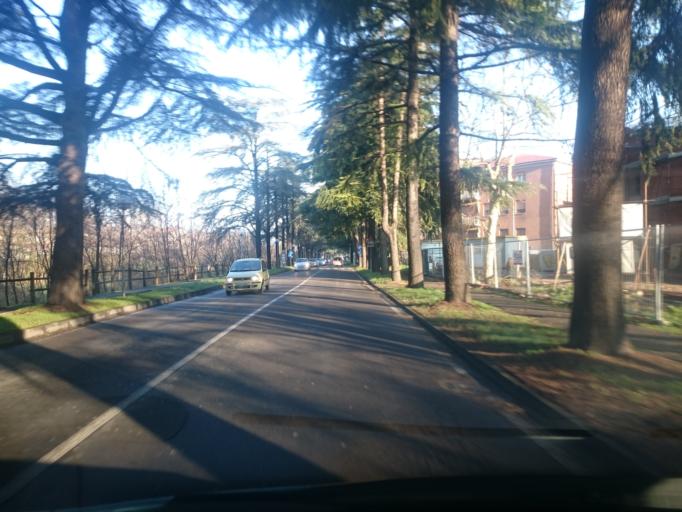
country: IT
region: Emilia-Romagna
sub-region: Provincia di Reggio Emilia
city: Reggio nell'Emilia
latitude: 44.6860
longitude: 10.6226
